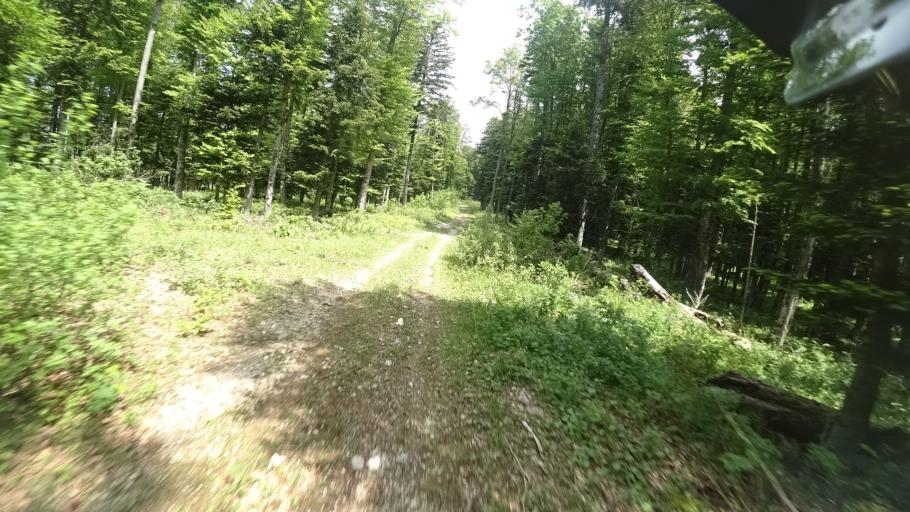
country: BA
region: Federation of Bosnia and Herzegovina
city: Orasac
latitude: 44.5686
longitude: 15.8647
